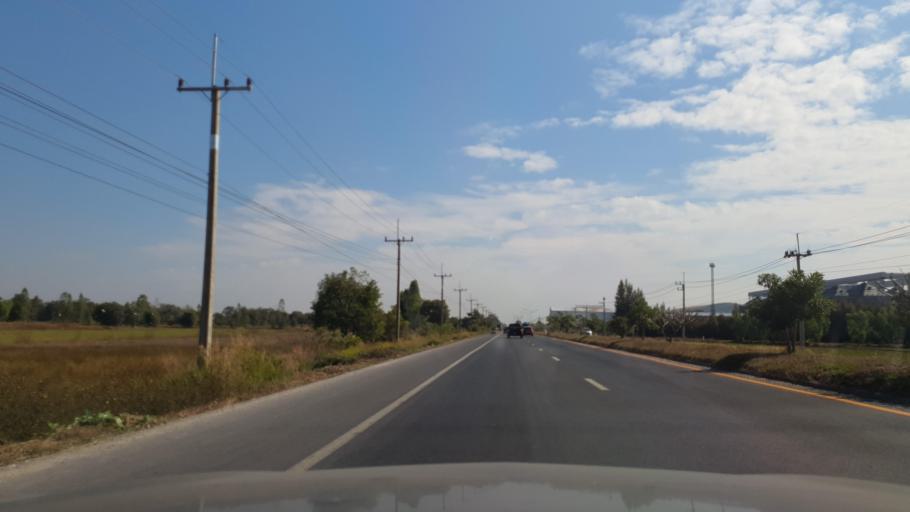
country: TH
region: Maha Sarakham
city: Kantharawichai
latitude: 16.3824
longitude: 103.2143
